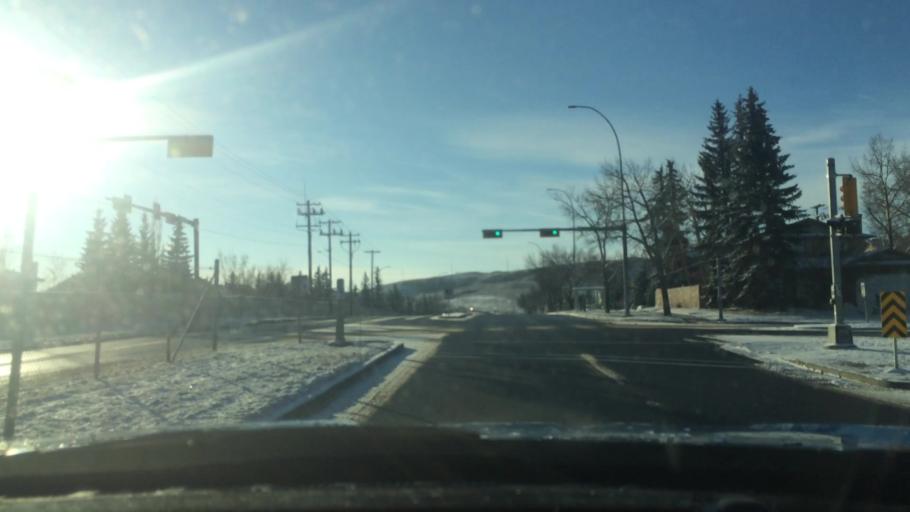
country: CA
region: Alberta
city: Calgary
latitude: 51.1352
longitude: -114.1074
